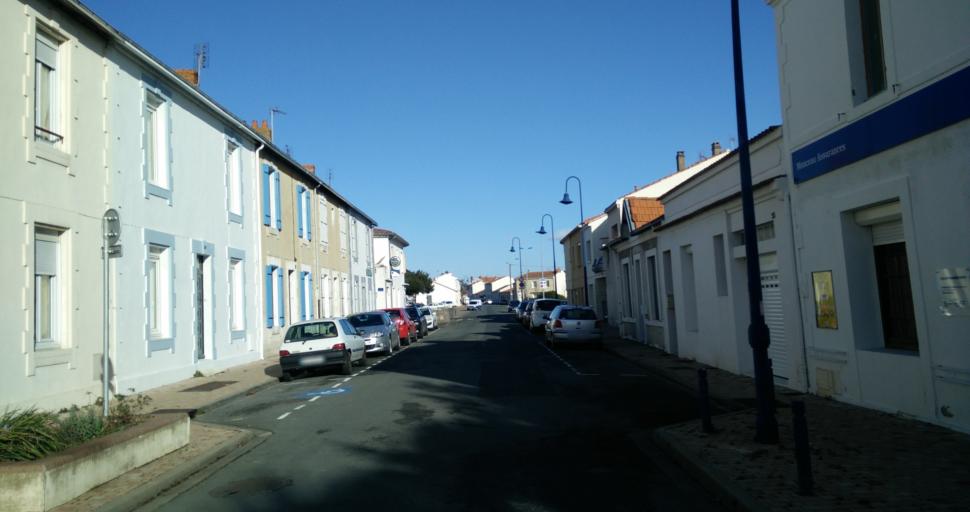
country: FR
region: Poitou-Charentes
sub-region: Departement de la Charente-Maritime
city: La Rochelle
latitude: 46.1620
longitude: -1.2064
